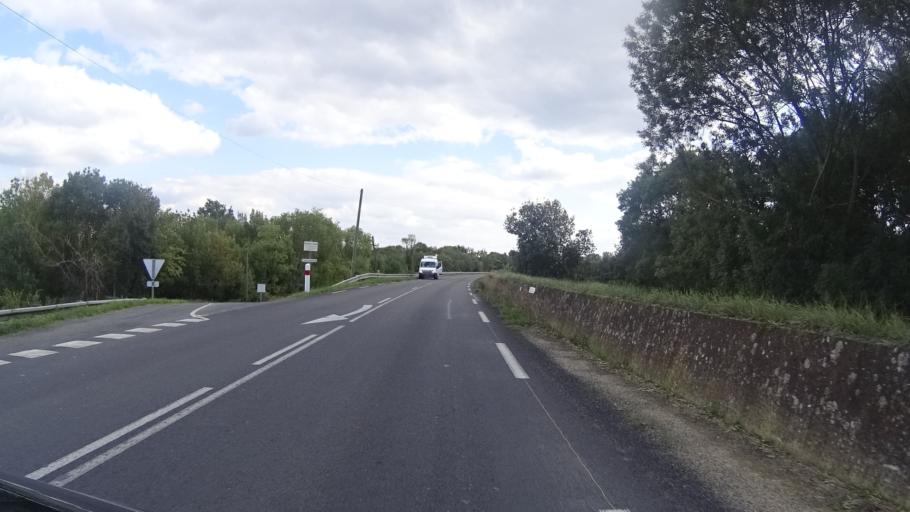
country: FR
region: Pays de la Loire
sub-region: Departement de Maine-et-Loire
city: Les Rosiers-sur-Loire
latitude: 47.3437
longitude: -0.2088
